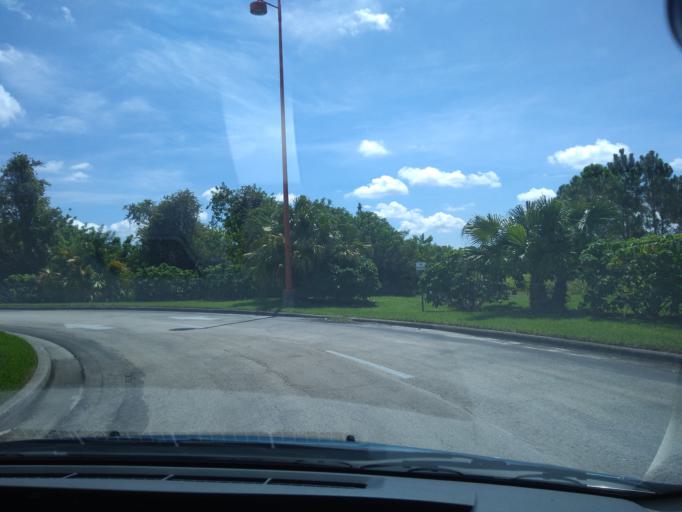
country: US
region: Florida
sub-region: Indian River County
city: West Vero Corridor
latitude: 27.6342
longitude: -80.5203
